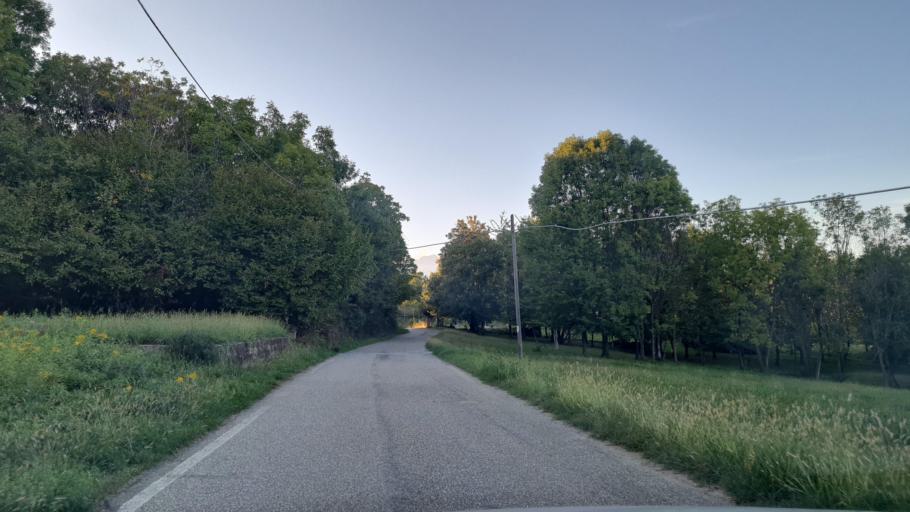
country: IT
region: Piedmont
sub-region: Provincia di Biella
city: Zubiena
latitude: 45.4871
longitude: 8.0075
